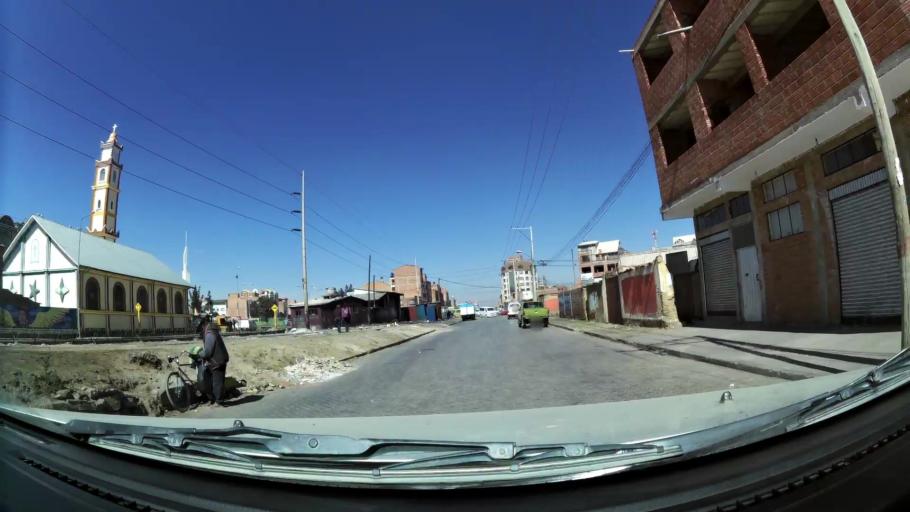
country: BO
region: La Paz
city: La Paz
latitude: -16.5148
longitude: -68.1551
